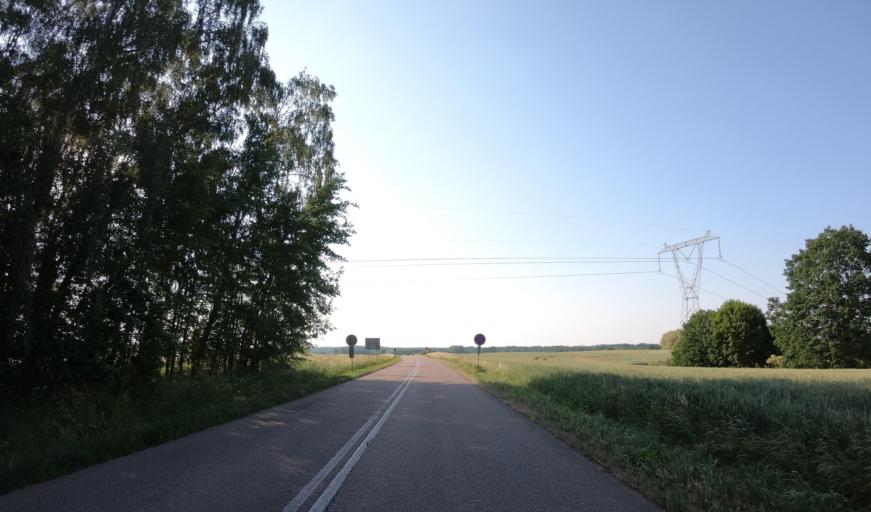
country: PL
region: West Pomeranian Voivodeship
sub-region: Powiat lobeski
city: Radowo Male
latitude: 53.6610
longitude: 15.4305
